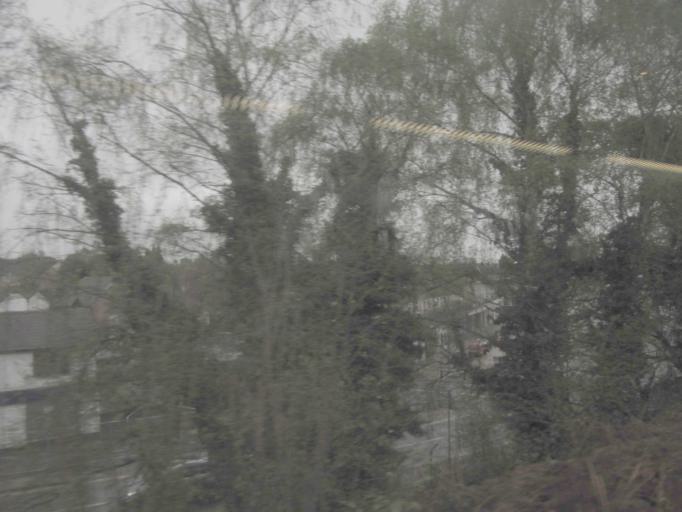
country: GB
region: England
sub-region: Bracknell Forest
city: Sandhurst
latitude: 51.3458
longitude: -0.8023
